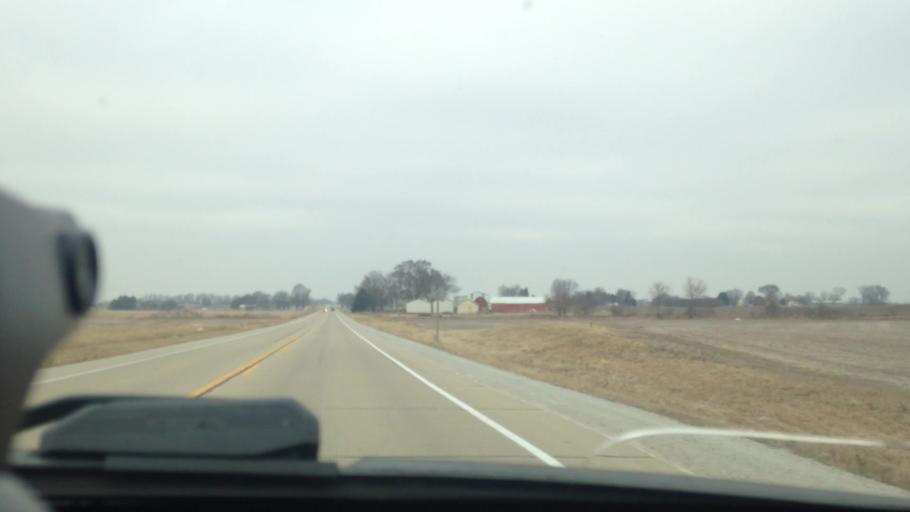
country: US
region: Wisconsin
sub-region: Dodge County
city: Beaver Dam
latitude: 43.4783
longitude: -88.7821
